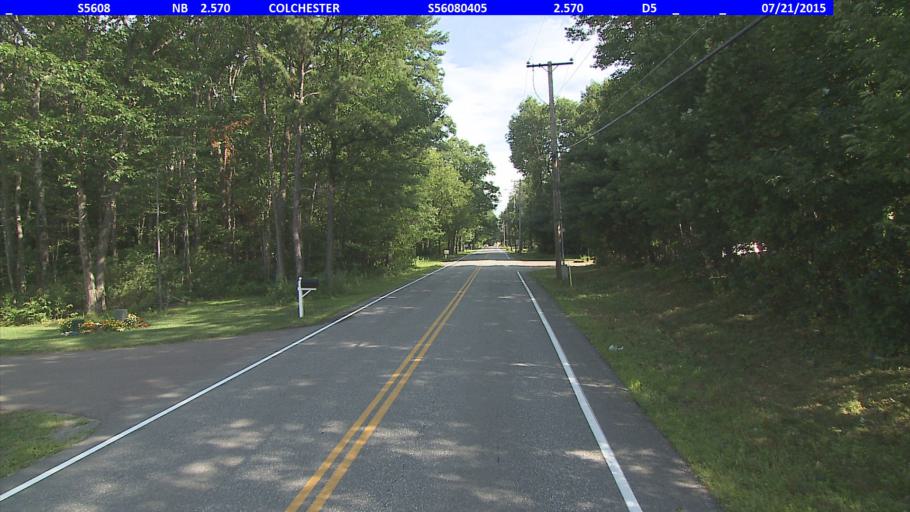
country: US
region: Vermont
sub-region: Chittenden County
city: Winooski
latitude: 44.5337
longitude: -73.2083
